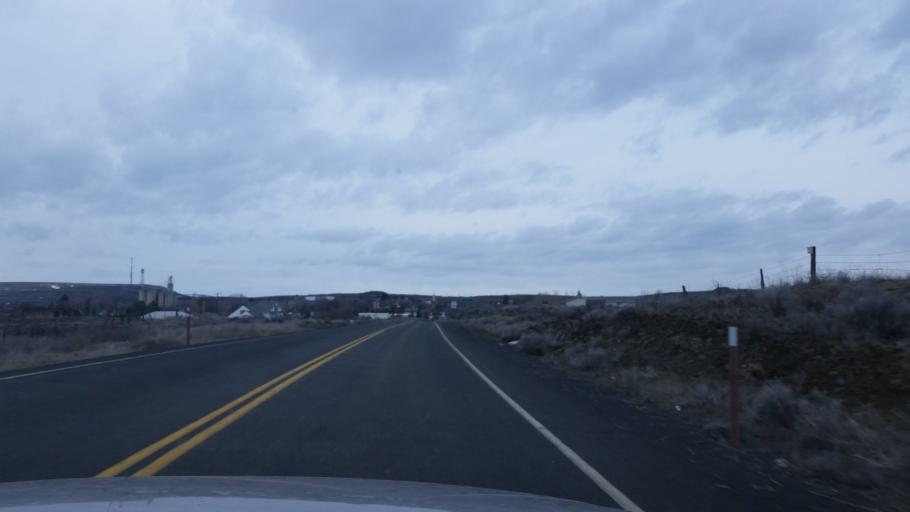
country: US
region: Washington
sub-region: Lincoln County
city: Davenport
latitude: 47.2926
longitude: -117.9721
